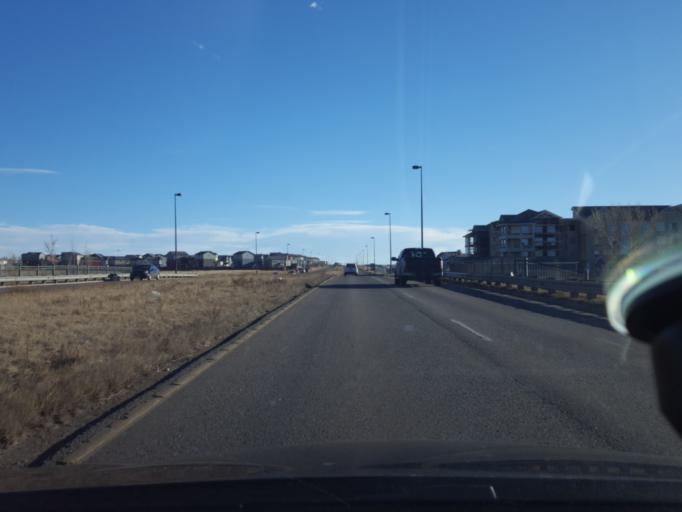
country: US
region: Colorado
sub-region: Adams County
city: Aurora
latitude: 39.7960
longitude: -104.7722
